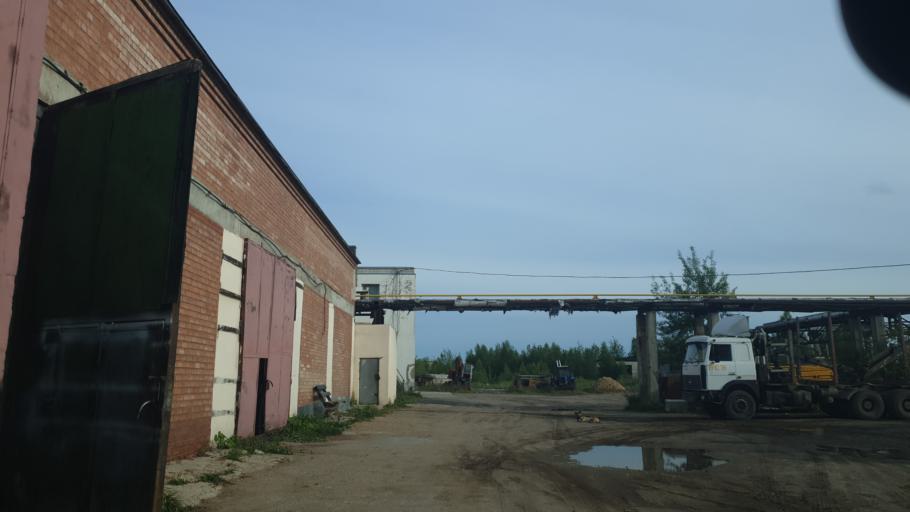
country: RU
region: Komi Republic
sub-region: Syktyvdinskiy Rayon
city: Syktyvkar
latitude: 61.7228
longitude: 50.7544
